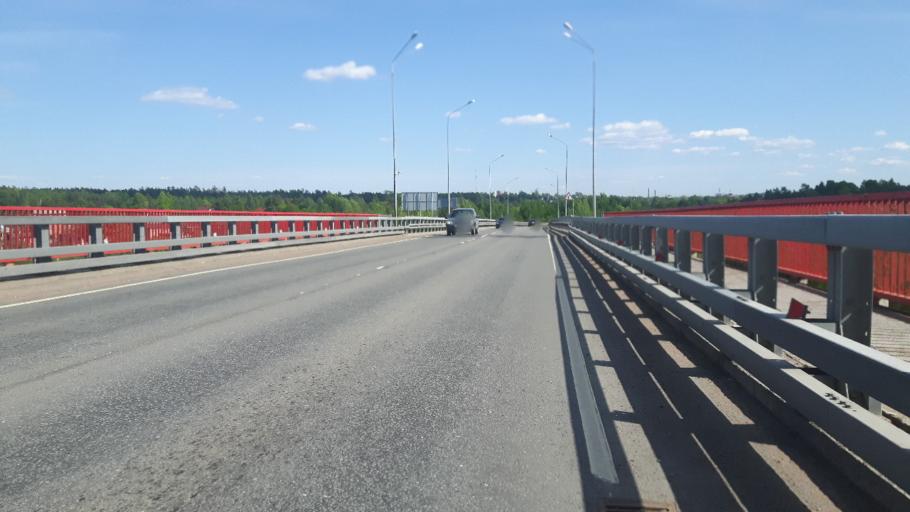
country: RU
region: Leningrad
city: Vyborg
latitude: 60.7368
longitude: 28.6926
